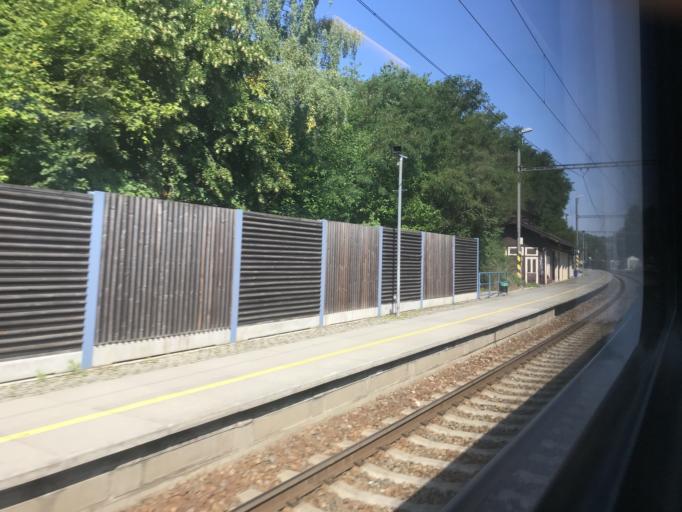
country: CZ
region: Central Bohemia
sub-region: Okres Praha-Vychod
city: Mnichovice
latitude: 49.9320
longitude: 14.7076
